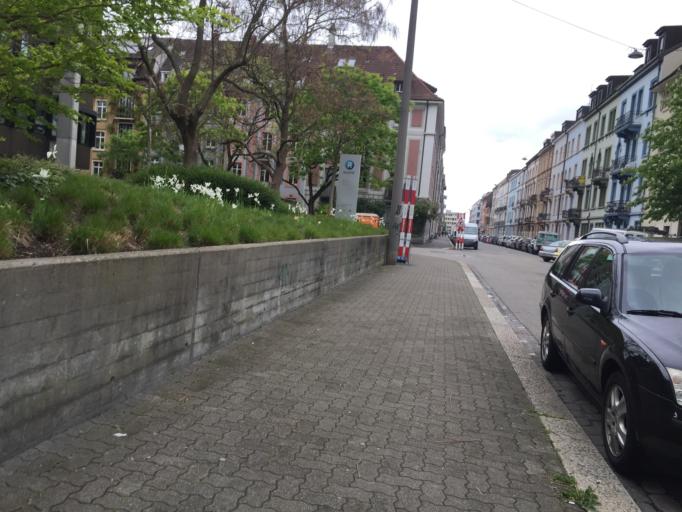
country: CH
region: Basel-Landschaft
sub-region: Bezirk Arlesheim
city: Birsfelden
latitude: 47.5437
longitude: 7.5978
